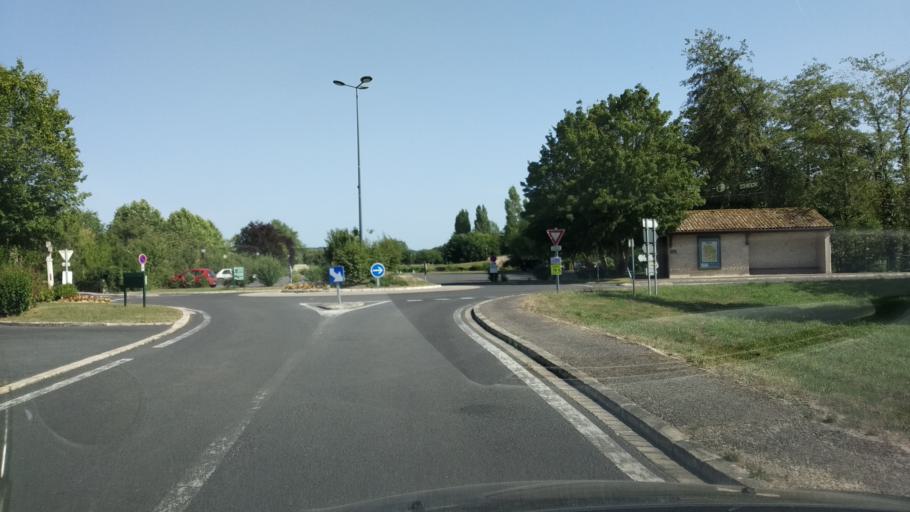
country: FR
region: Poitou-Charentes
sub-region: Departement de la Vienne
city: Lussac-les-Chateaux
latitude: 46.4450
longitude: 0.6616
